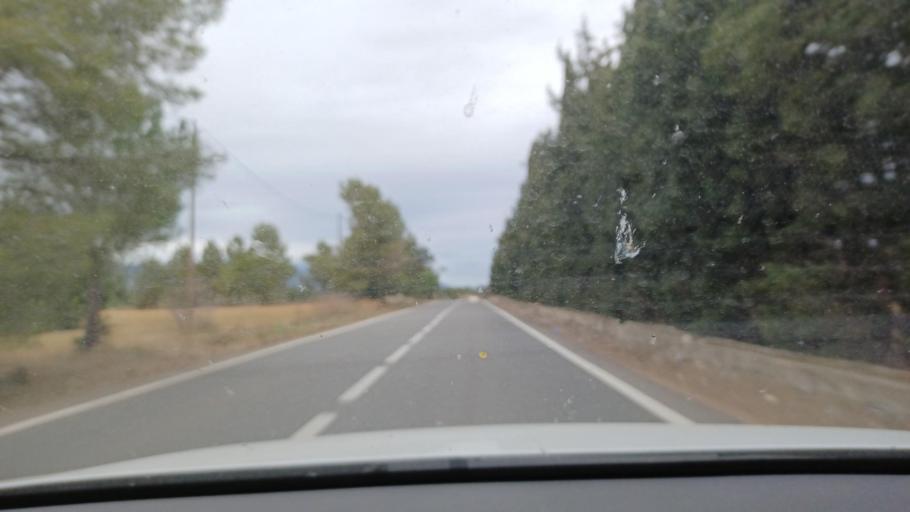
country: ES
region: Catalonia
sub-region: Provincia de Tarragona
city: Ulldecona
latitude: 40.6114
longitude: 0.3497
